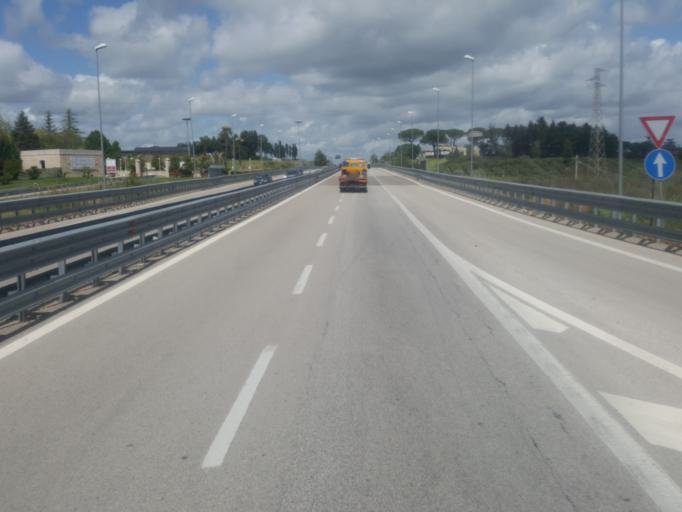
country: IT
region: Basilicate
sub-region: Provincia di Matera
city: Matera
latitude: 40.6977
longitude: 16.5898
